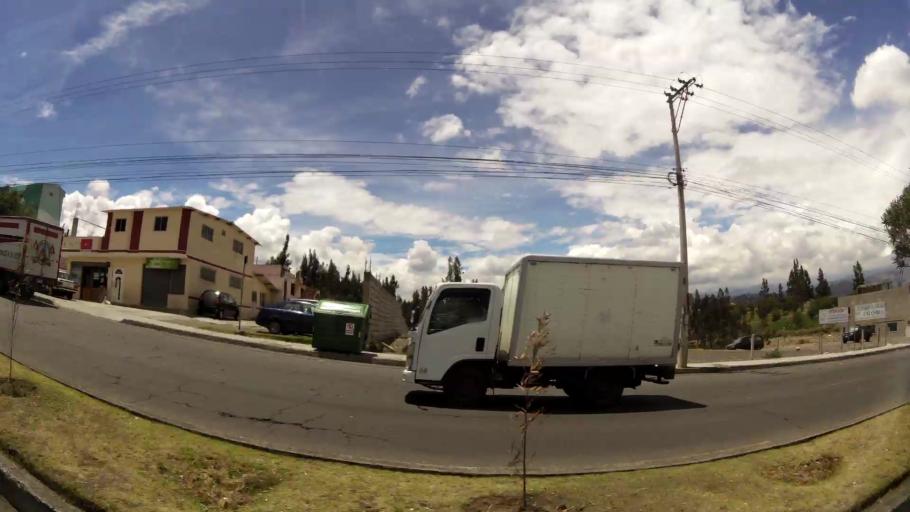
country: EC
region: Tungurahua
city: Ambato
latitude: -1.2963
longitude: -78.6014
